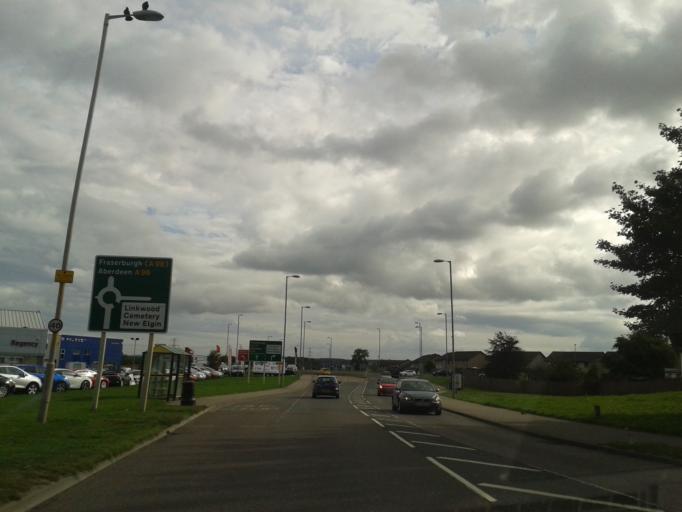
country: GB
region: Scotland
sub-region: Moray
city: Elgin
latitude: 57.6460
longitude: -3.2843
